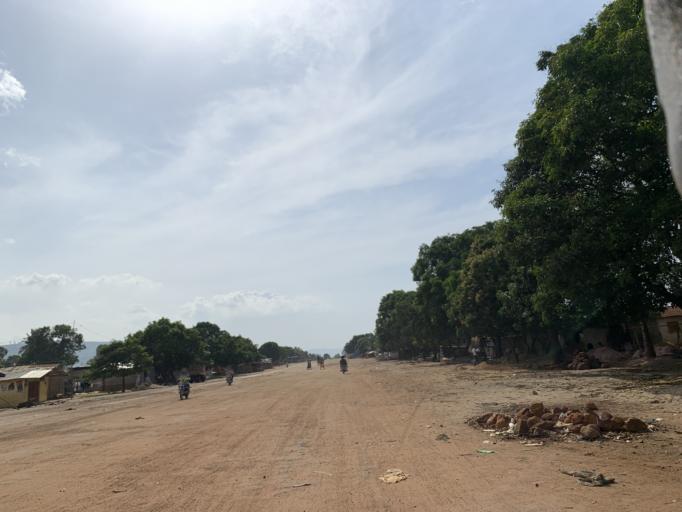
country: SL
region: Western Area
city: Waterloo
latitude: 8.3386
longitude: -13.0452
